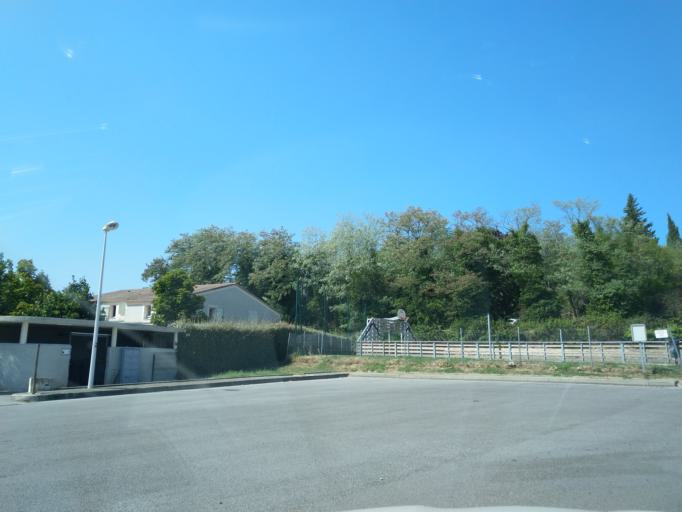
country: FR
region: Rhone-Alpes
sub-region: Departement de l'Ardeche
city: Ruoms
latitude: 44.4107
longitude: 4.4005
